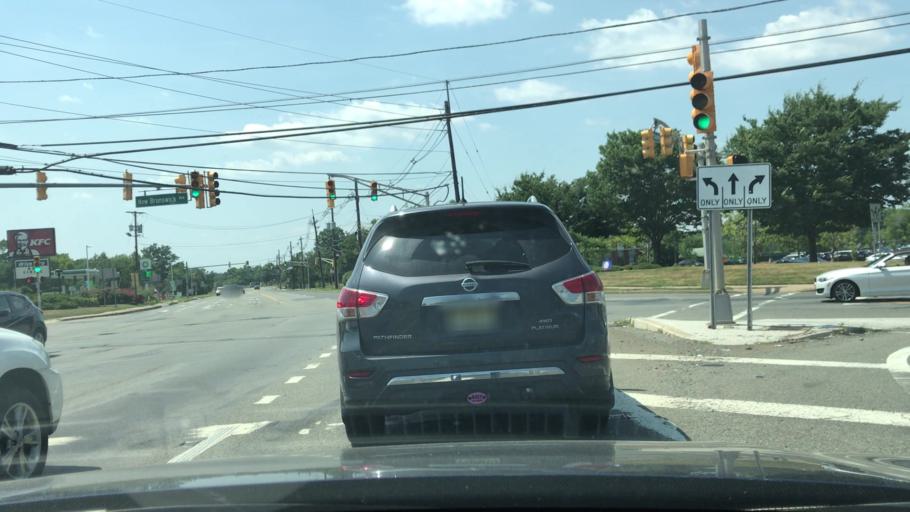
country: US
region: New Jersey
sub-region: Middlesex County
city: Society Hill
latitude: 40.5594
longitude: -74.4393
